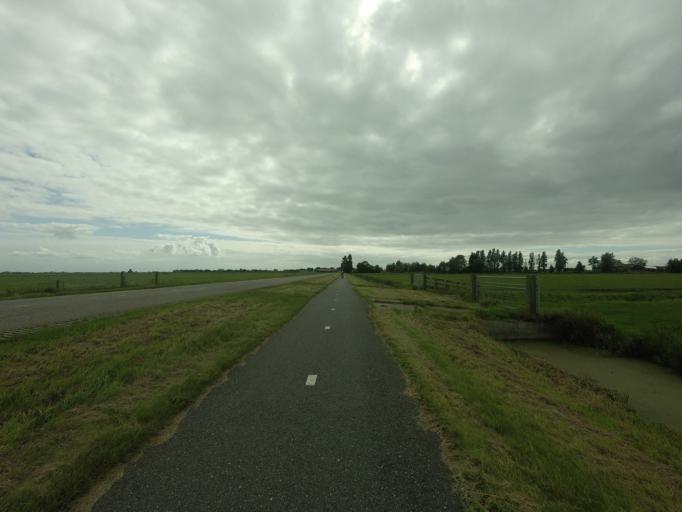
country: NL
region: Friesland
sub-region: Sudwest Fryslan
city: Heeg
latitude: 52.9789
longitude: 5.5432
